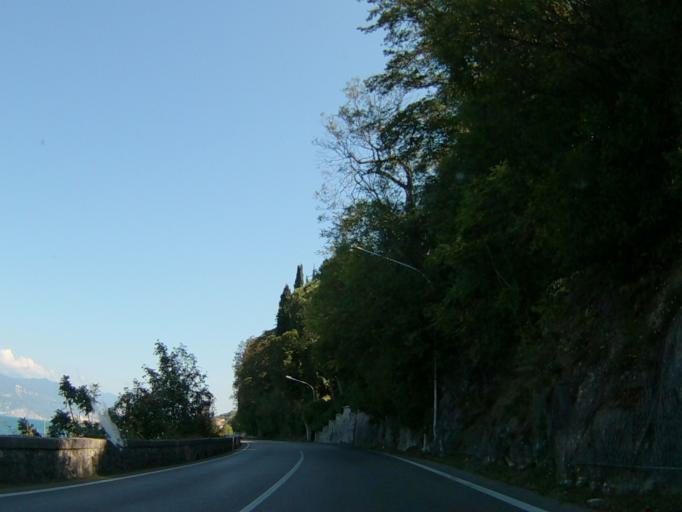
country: IT
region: Veneto
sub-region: Provincia di Verona
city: Torri del Benaco
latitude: 45.5942
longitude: 10.6817
